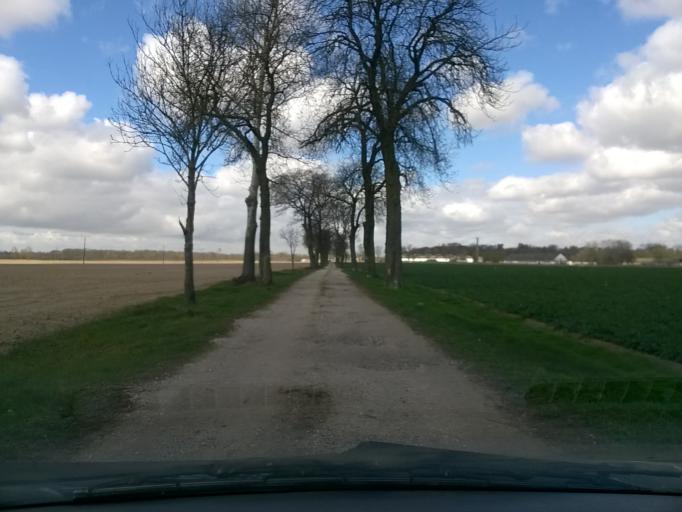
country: PL
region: Kujawsko-Pomorskie
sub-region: Powiat nakielski
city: Kcynia
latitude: 52.9843
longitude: 17.4338
